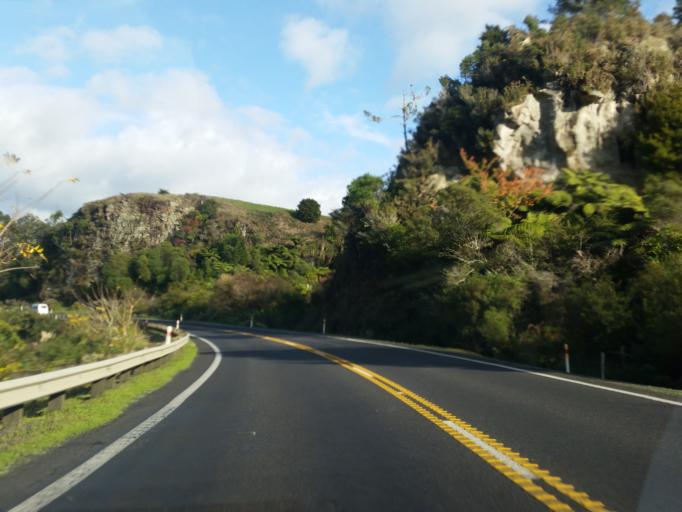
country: NZ
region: Waikato
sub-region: Hauraki District
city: Waihi
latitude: -37.4134
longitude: 175.7937
